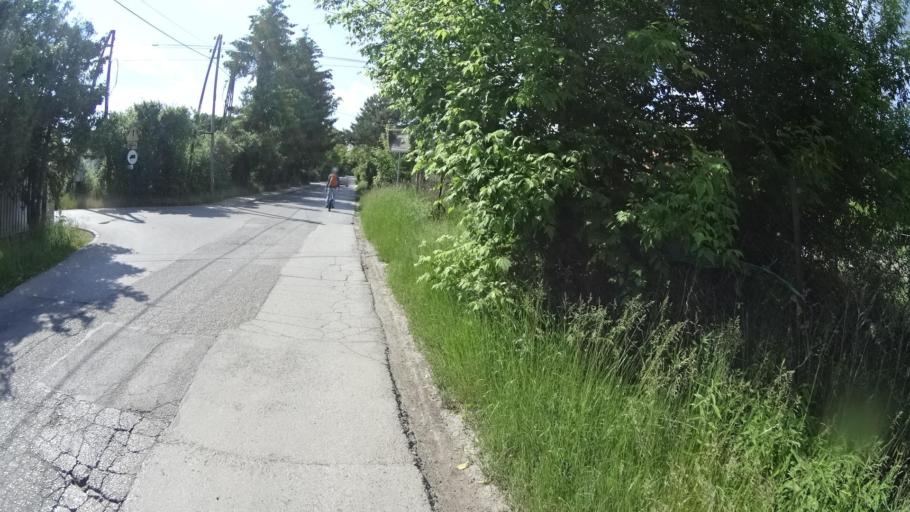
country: PL
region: Masovian Voivodeship
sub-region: Powiat piaseczynski
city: Jozefoslaw
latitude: 52.1125
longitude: 21.0340
